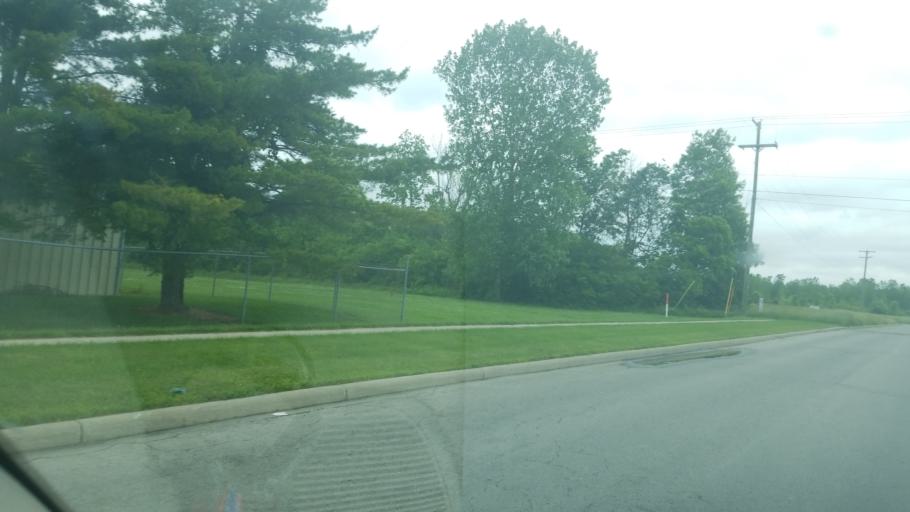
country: US
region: Ohio
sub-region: Marion County
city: Marion
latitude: 40.5693
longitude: -83.1176
